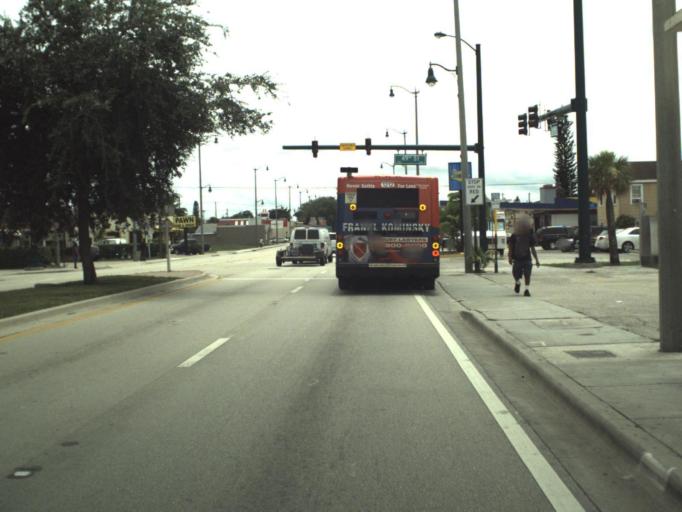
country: US
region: Florida
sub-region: Palm Beach County
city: Mangonia Park
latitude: 26.7562
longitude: -80.0559
